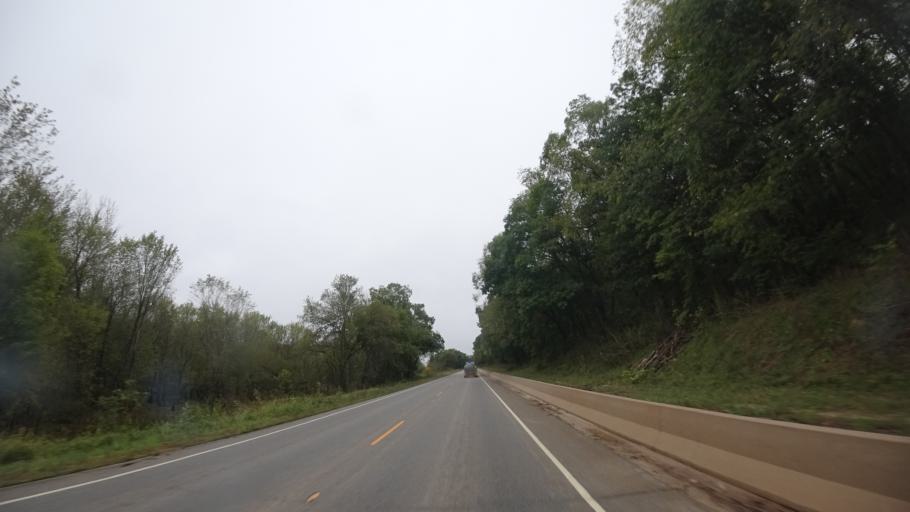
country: US
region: Wisconsin
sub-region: Crawford County
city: Prairie du Chien
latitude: 43.0579
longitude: -90.9622
